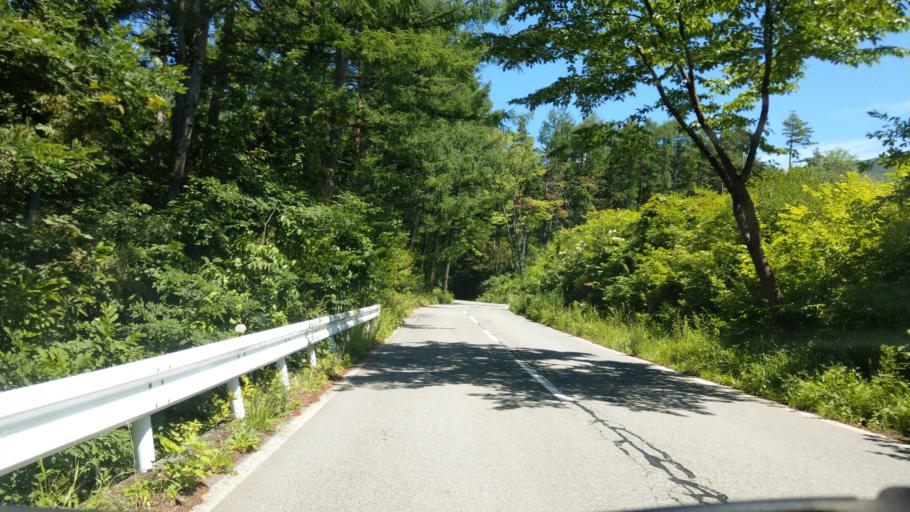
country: JP
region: Nagano
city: Komoro
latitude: 36.3824
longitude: 138.4620
